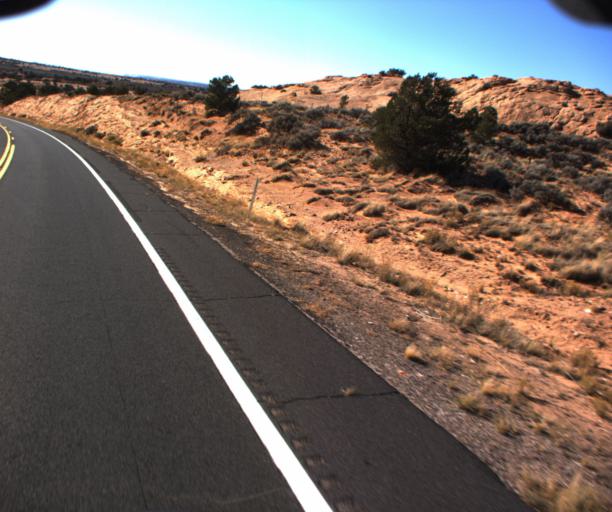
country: US
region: Arizona
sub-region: Coconino County
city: Kaibito
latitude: 36.5634
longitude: -110.7375
